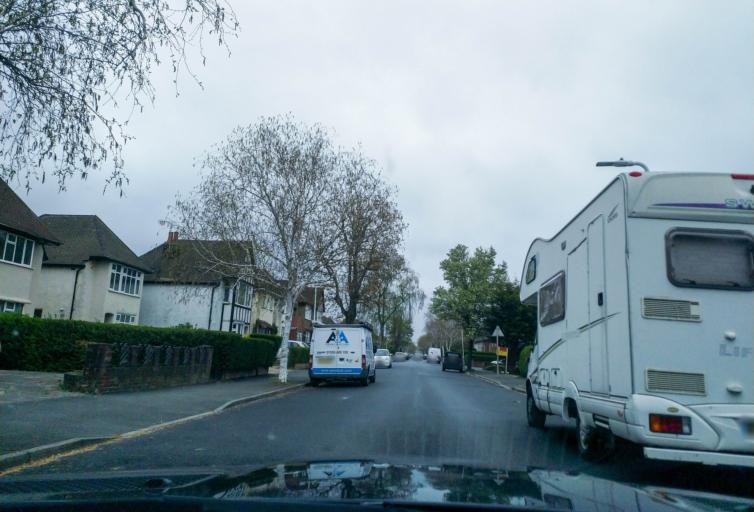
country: GB
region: England
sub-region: Greater London
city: Northolt
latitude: 51.5629
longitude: -0.3920
